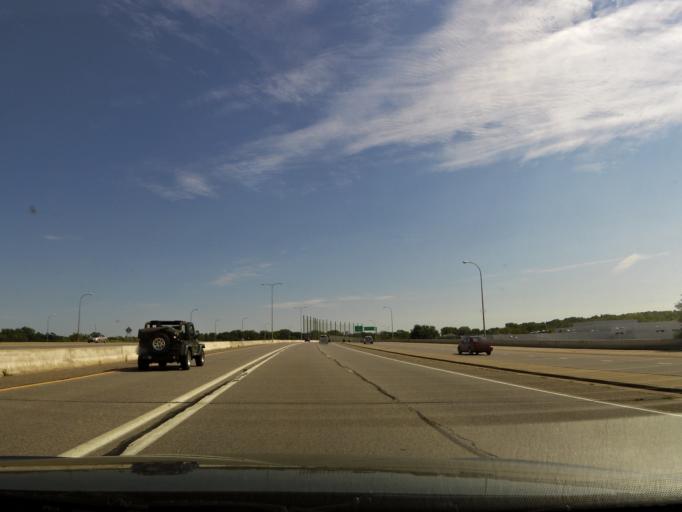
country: US
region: Minnesota
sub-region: Hennepin County
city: Saint Louis Park
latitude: 44.9739
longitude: -93.3949
